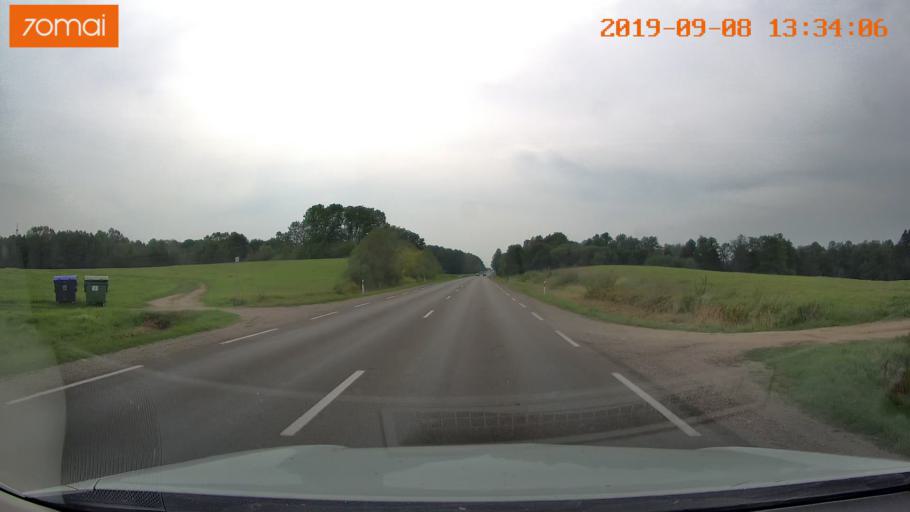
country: LT
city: Jieznas
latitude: 54.5013
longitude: 24.1360
